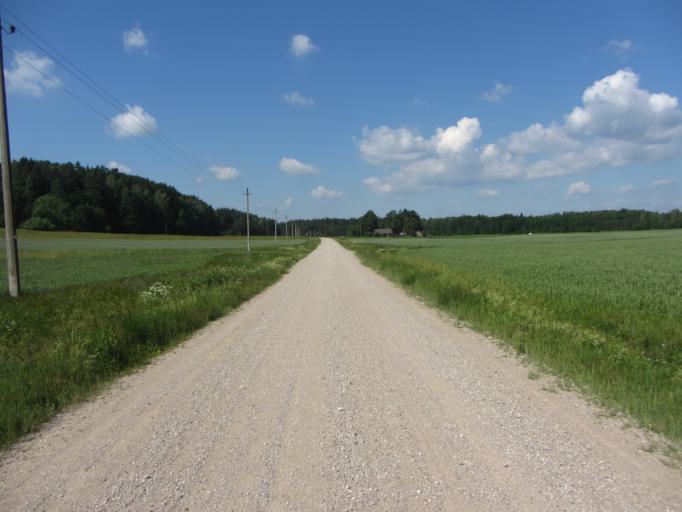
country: LT
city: Prienai
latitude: 54.5449
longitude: 23.9367
